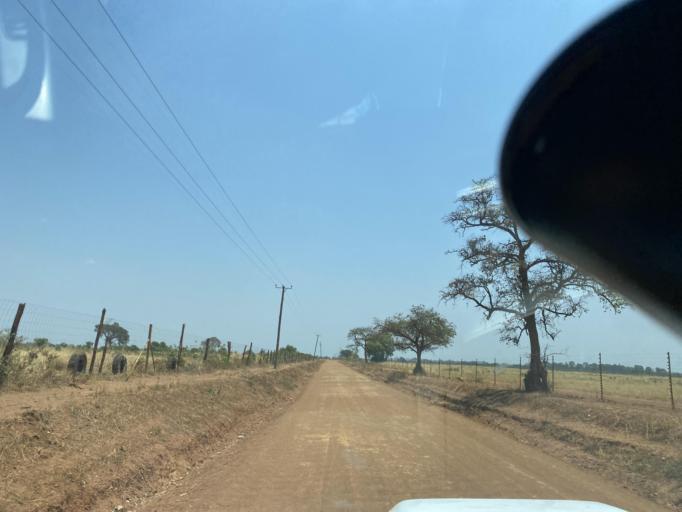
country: ZM
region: Lusaka
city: Lusaka
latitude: -15.4416
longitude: 28.0533
